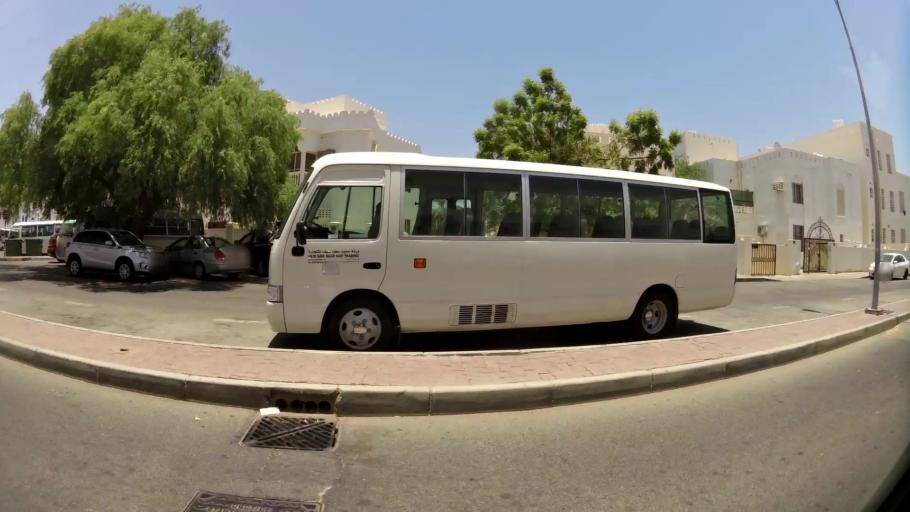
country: OM
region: Muhafazat Masqat
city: Muscat
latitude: 23.6179
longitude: 58.5388
